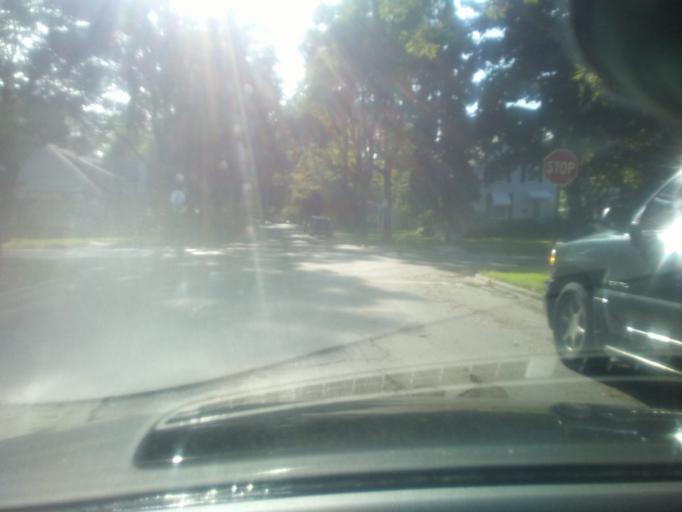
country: US
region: Illinois
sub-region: Cook County
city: Evanston
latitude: 42.0392
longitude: -87.7051
